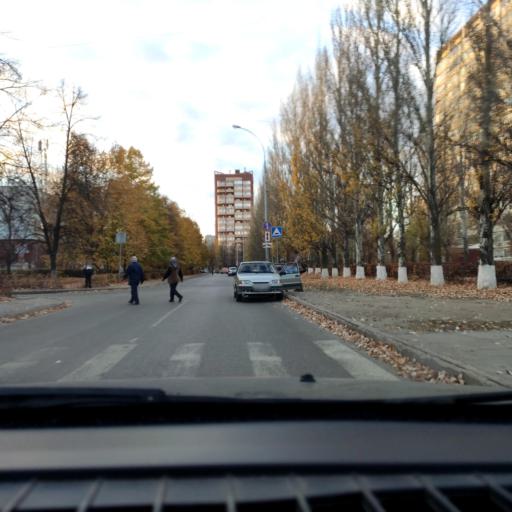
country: RU
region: Samara
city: Tol'yatti
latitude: 53.5289
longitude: 49.3039
